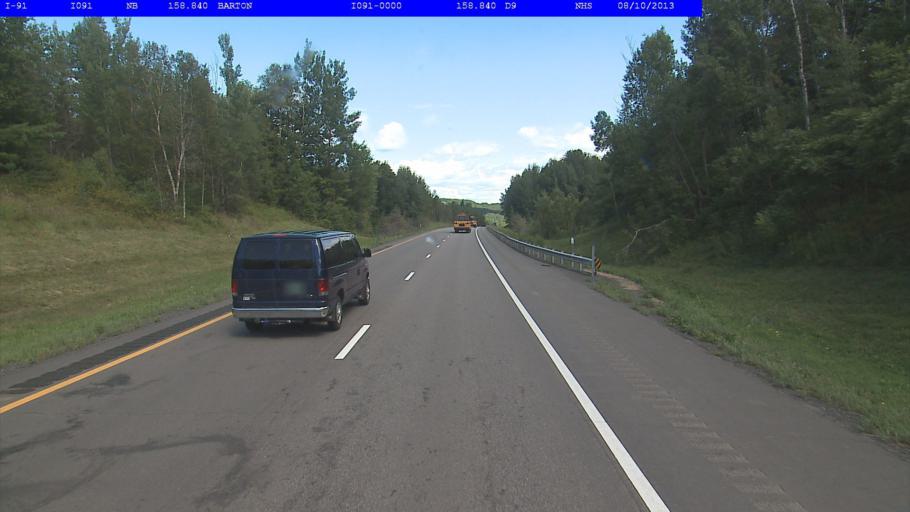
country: US
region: Vermont
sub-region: Orleans County
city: Newport
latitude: 44.7697
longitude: -72.2130
